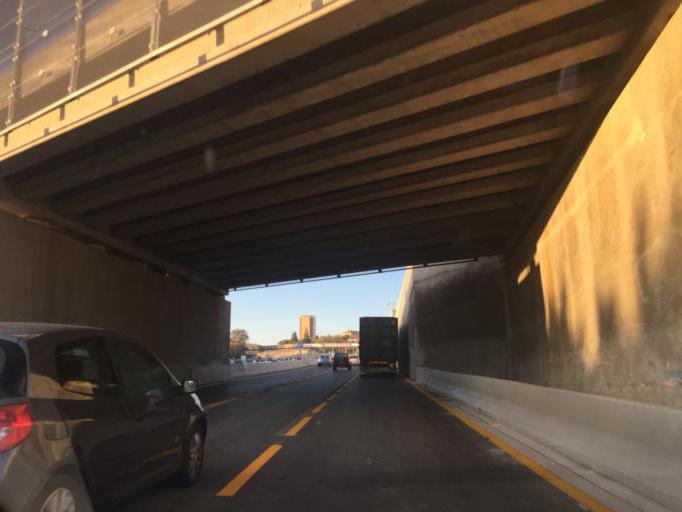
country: FR
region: Provence-Alpes-Cote d'Azur
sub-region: Departement des Bouches-du-Rhone
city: Marseille 14
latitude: 43.3411
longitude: 5.3765
